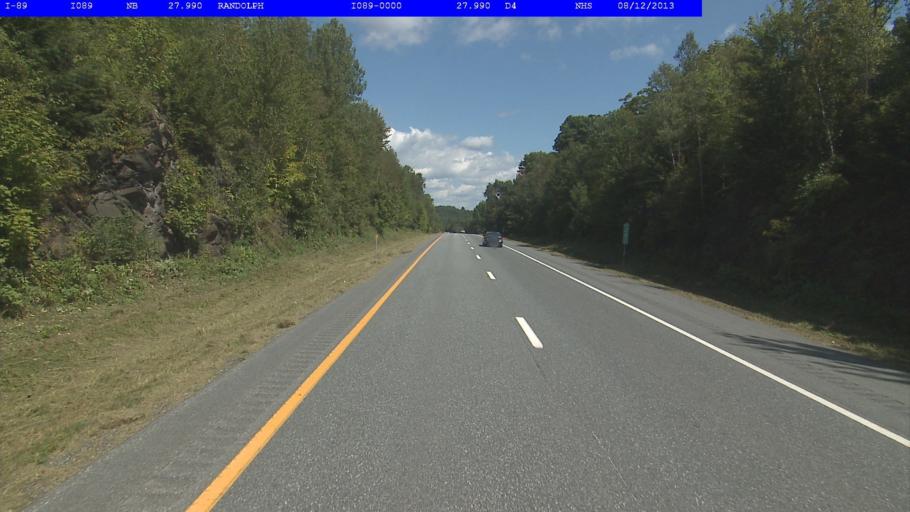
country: US
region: Vermont
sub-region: Orange County
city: Randolph
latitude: 43.9034
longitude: -72.6140
